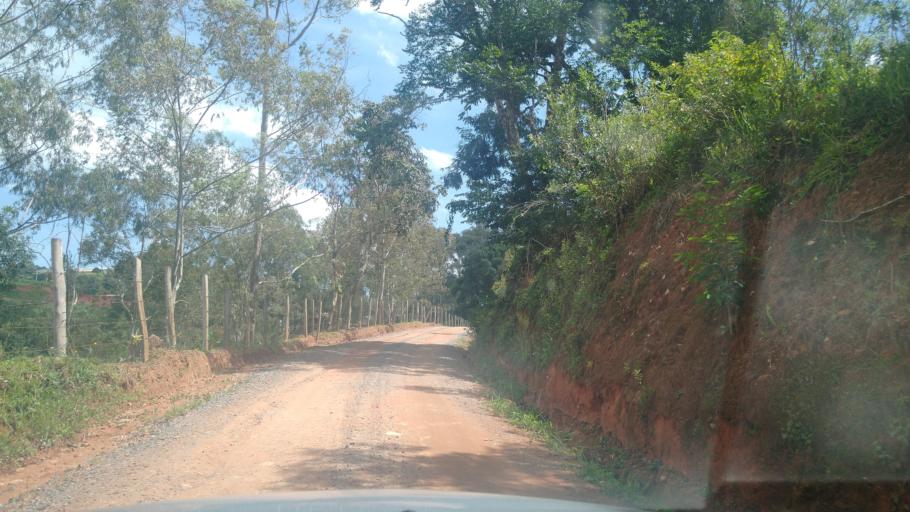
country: BR
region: Minas Gerais
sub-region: Extrema
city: Extrema
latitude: -22.7388
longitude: -46.2953
